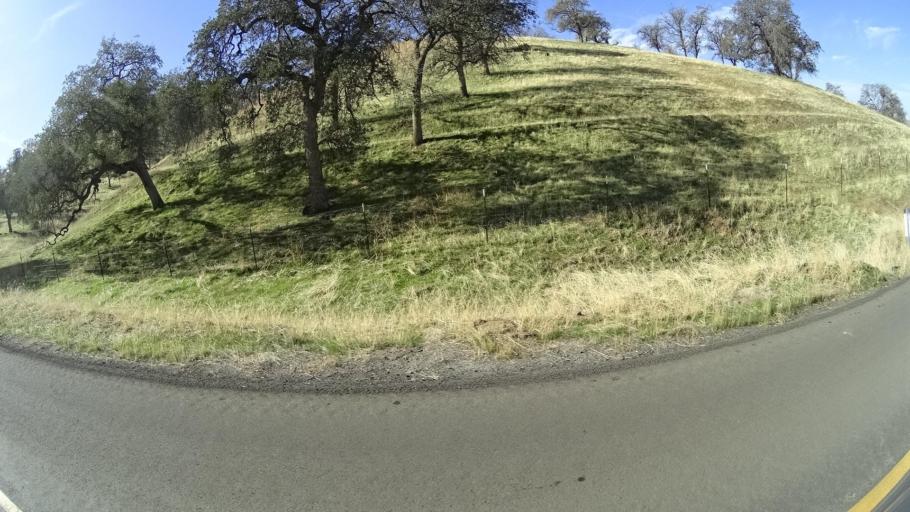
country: US
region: California
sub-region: Kern County
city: Alta Sierra
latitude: 35.6929
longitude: -118.8351
